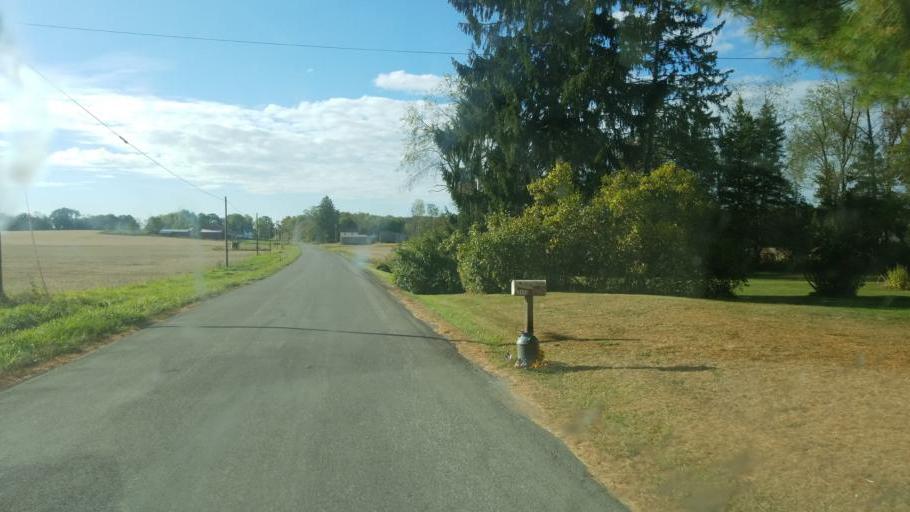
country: US
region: Pennsylvania
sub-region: Mercer County
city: Mercer
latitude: 41.3596
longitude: -80.2472
